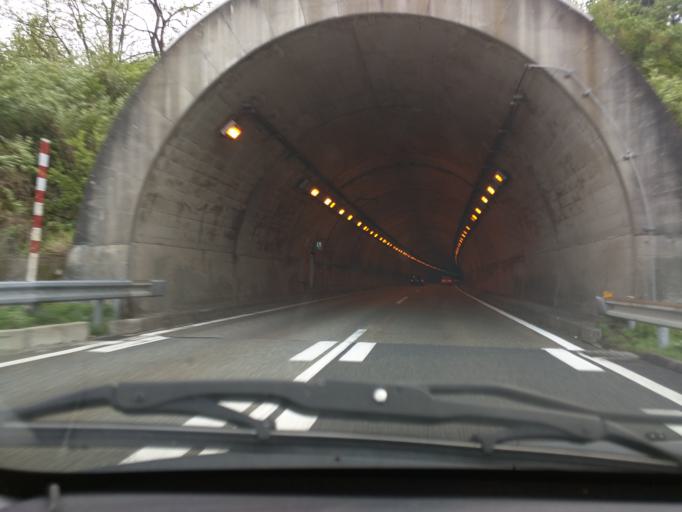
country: JP
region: Niigata
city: Muikamachi
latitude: 37.1973
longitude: 138.9610
